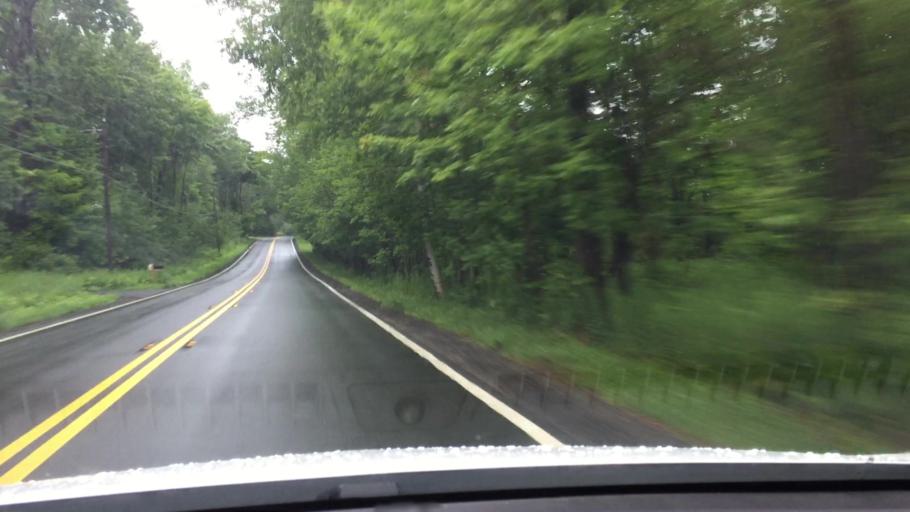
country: US
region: Massachusetts
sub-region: Berkshire County
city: Becket
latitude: 42.3404
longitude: -73.1122
